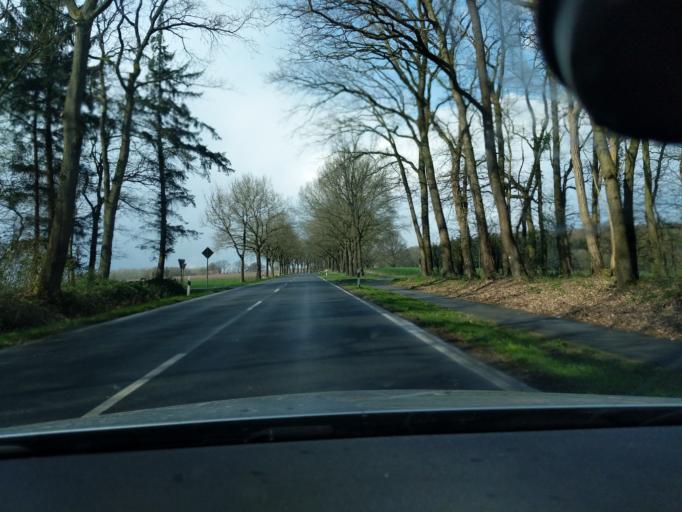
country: DE
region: Lower Saxony
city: Harsefeld
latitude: 53.4681
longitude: 9.4955
